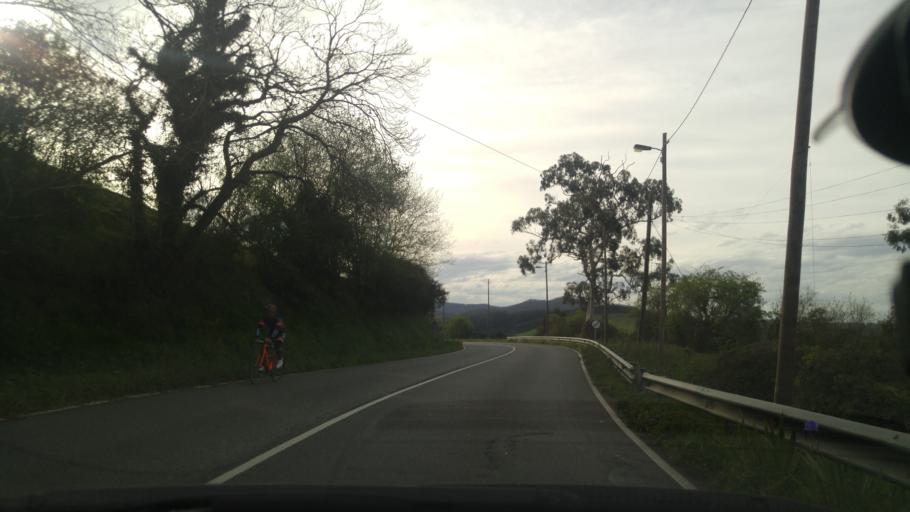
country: ES
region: Asturias
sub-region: Province of Asturias
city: Corvera de Asturias
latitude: 43.4766
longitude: -5.8450
